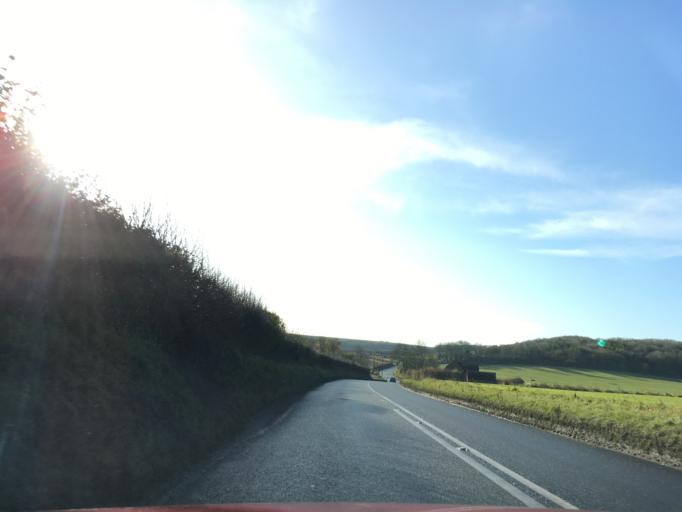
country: GB
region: England
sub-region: Wiltshire
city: Burbage
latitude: 51.3324
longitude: -1.6763
